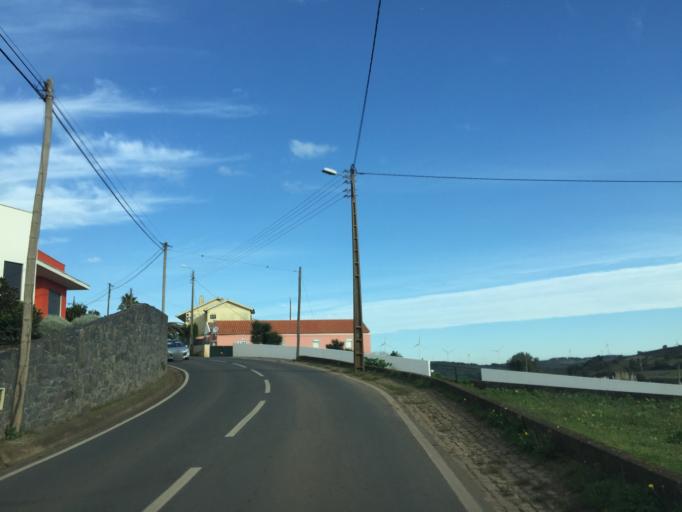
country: PT
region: Lisbon
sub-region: Sintra
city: Almargem
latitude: 38.8360
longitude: -9.2534
